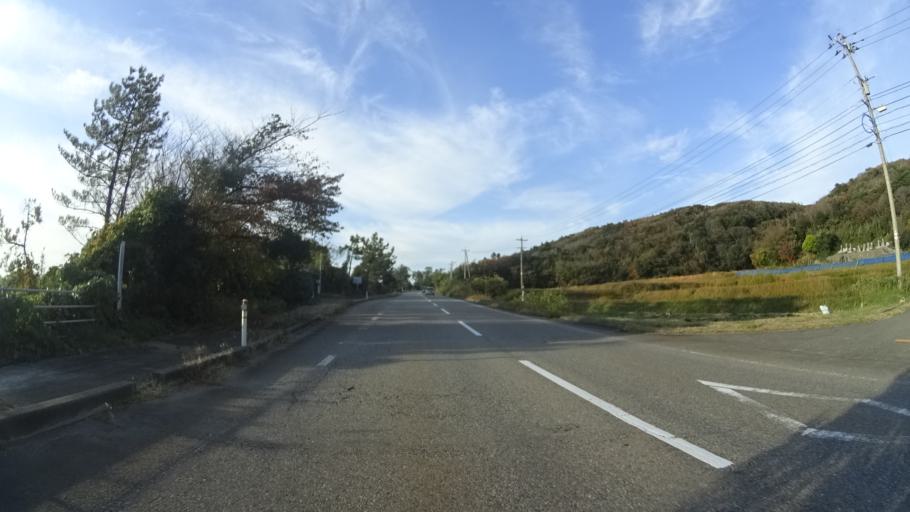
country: JP
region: Ishikawa
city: Hakui
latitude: 37.1048
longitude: 136.7298
